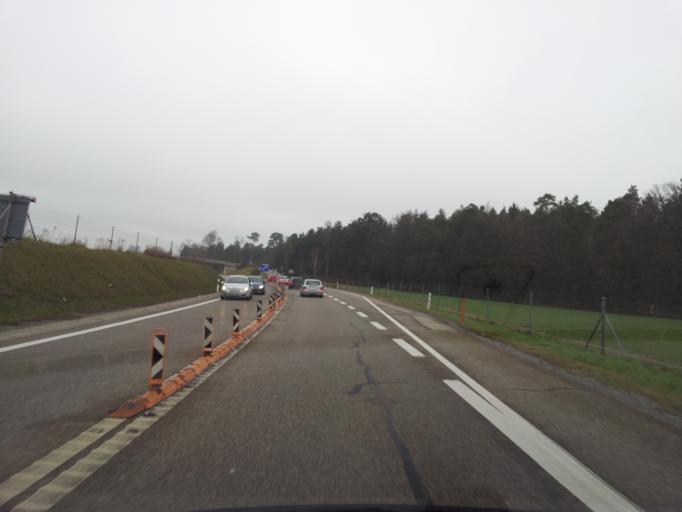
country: CH
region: Zurich
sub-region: Bezirk Andelfingen
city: Henggart
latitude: 47.5614
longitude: 8.6918
